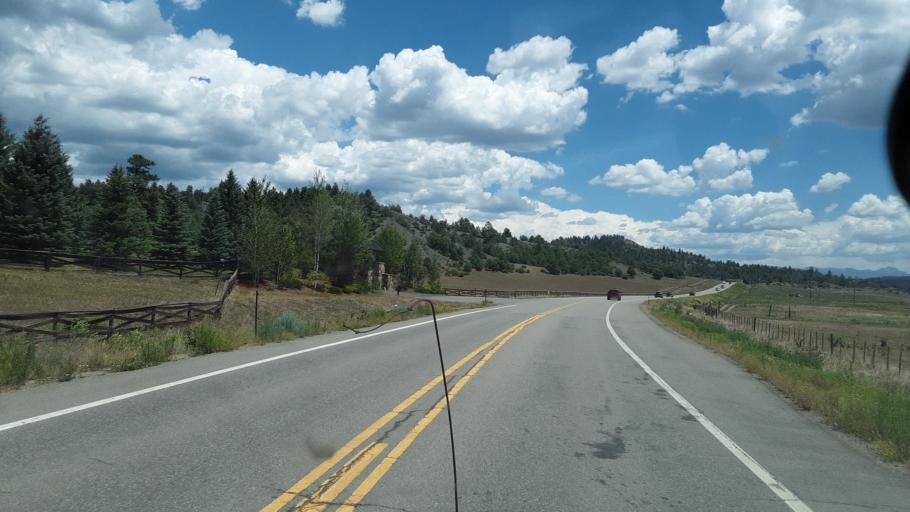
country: US
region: Colorado
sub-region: Archuleta County
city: Pagosa Springs
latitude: 37.2264
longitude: -107.2132
